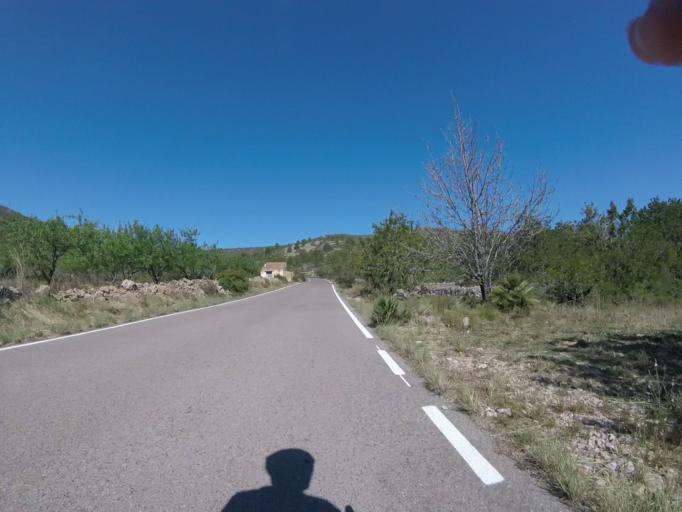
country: ES
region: Valencia
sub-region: Provincia de Castello
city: Santa Magdalena de Pulpis
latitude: 40.3827
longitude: 0.2621
